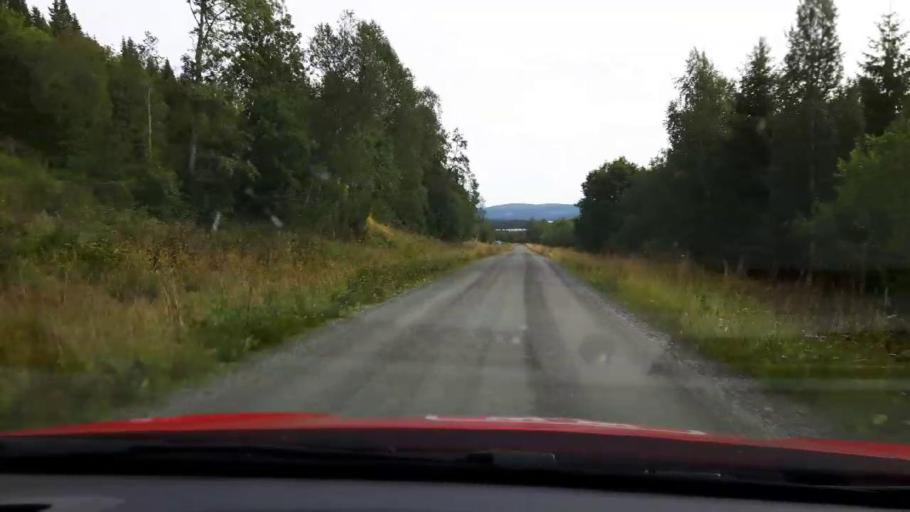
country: SE
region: Jaemtland
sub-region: Are Kommun
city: Are
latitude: 63.7466
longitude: 12.9714
